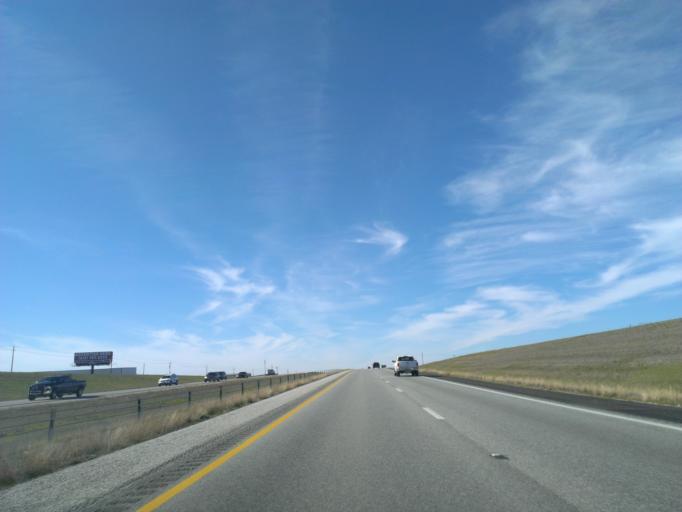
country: US
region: Texas
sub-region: Bell County
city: Nolanville
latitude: 31.0695
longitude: -97.5851
